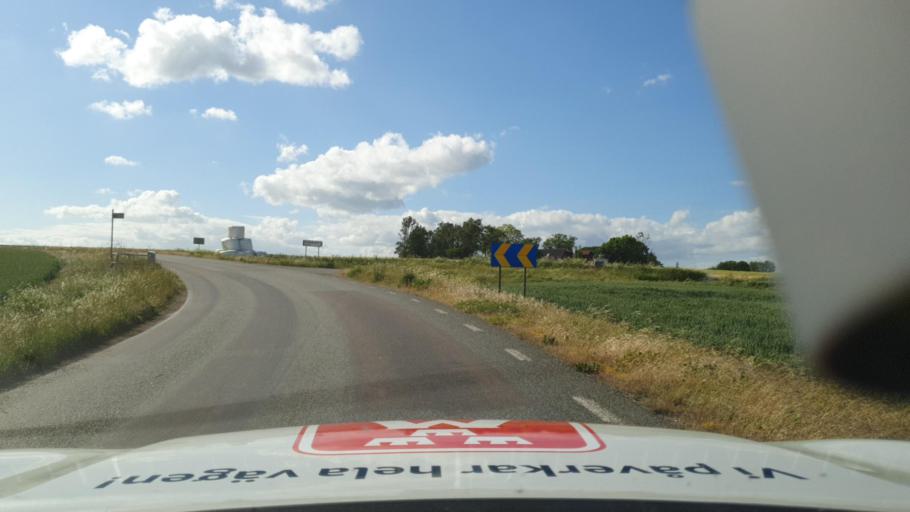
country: SE
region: Skane
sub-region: Simrishamns Kommun
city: Simrishamn
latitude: 55.5636
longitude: 14.3056
